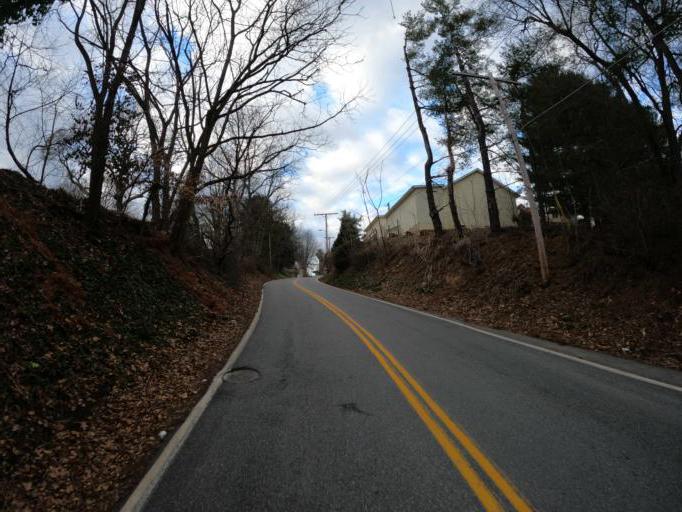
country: US
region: Maryland
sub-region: Carroll County
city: Sykesville
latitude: 39.3729
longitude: -76.9710
